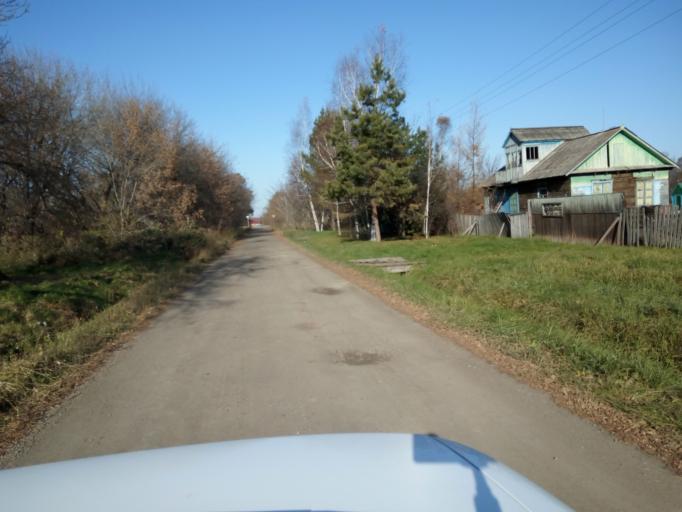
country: RU
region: Primorskiy
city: Lazo
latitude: 45.8696
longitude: 133.6480
